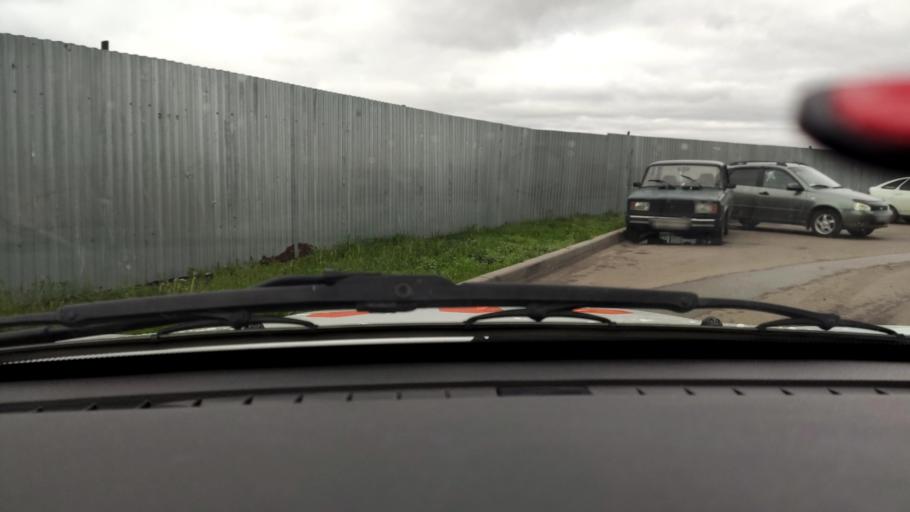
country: RU
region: Voronezj
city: Novaya Usman'
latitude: 51.6113
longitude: 39.3692
